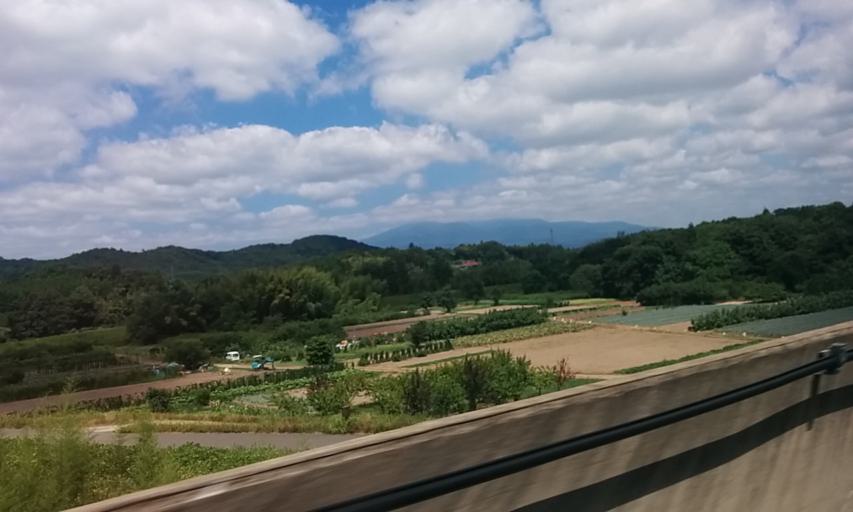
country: JP
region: Fukushima
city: Motomiya
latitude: 37.4647
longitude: 140.4116
